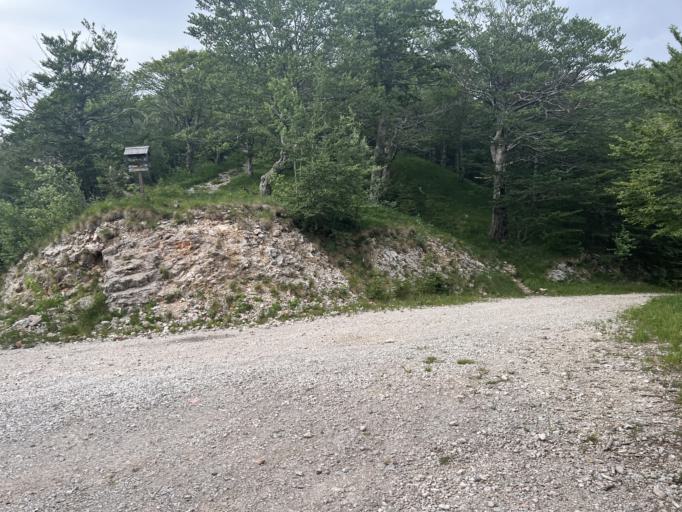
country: HR
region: Primorsko-Goranska
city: Krasica
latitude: 45.4206
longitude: 14.6056
